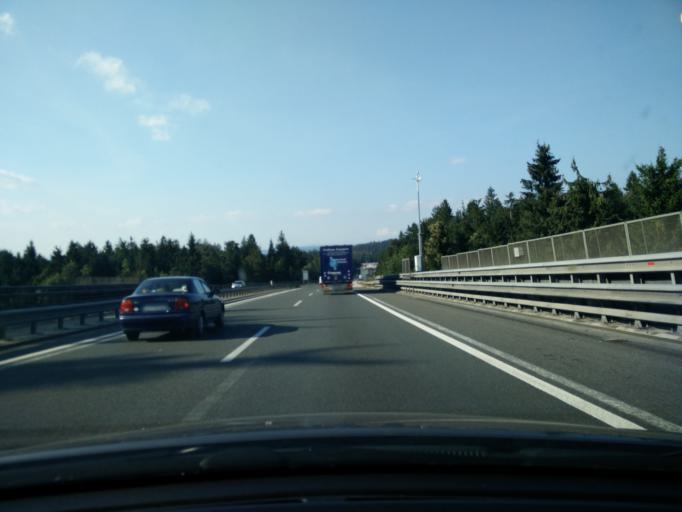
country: SI
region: Logatec
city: Logatec
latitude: 45.8905
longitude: 14.2580
